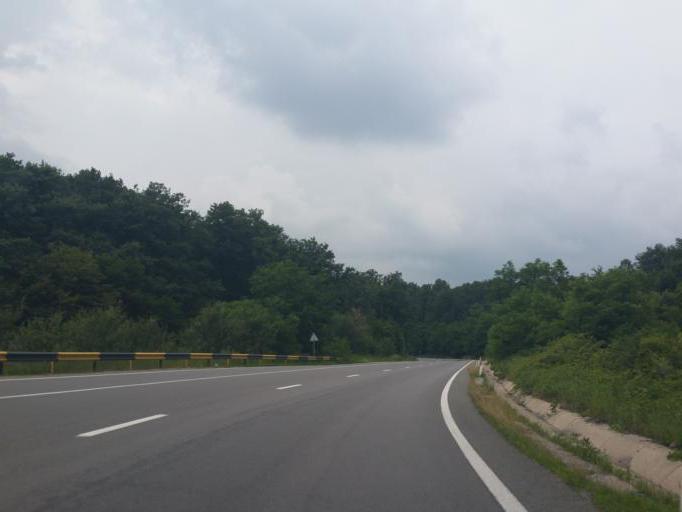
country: RO
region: Salaj
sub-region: Comuna Treznea
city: Treznea
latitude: 47.1371
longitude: 23.1195
